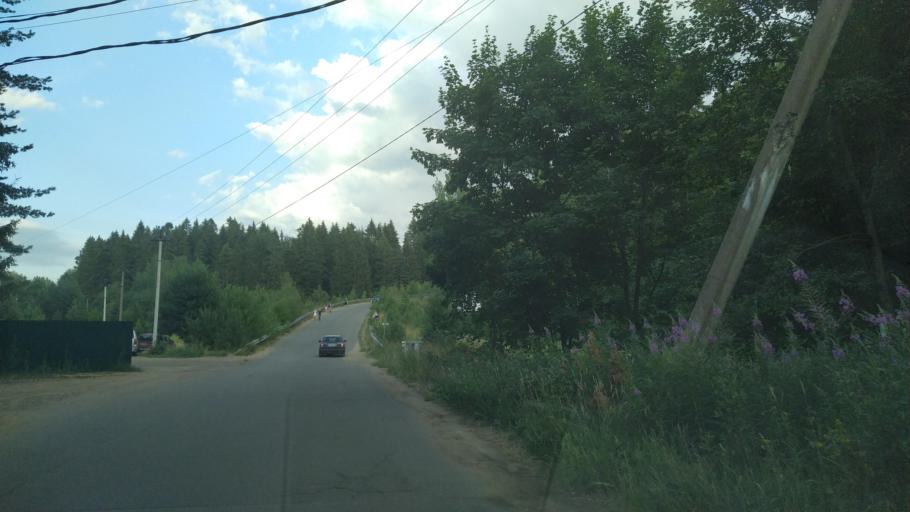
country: RU
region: Leningrad
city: Toksovo
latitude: 60.1680
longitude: 30.5333
